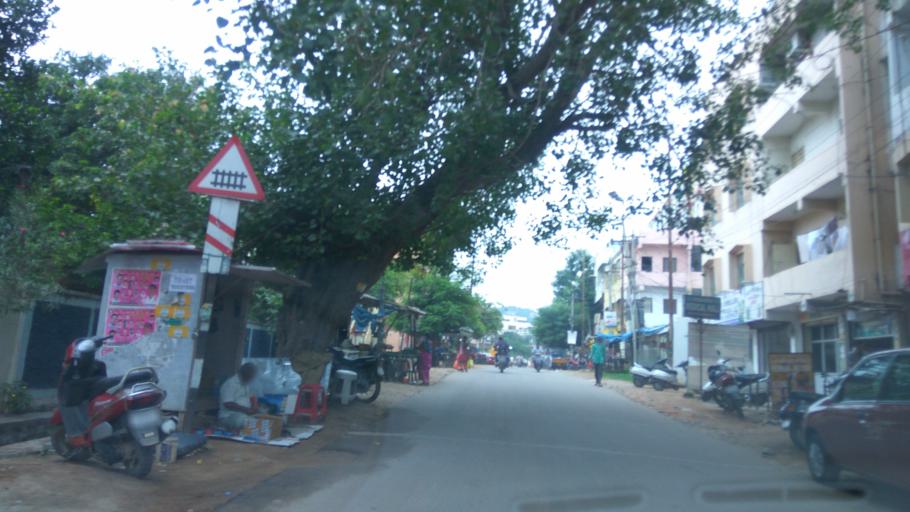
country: IN
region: Telangana
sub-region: Hyderabad
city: Malkajgiri
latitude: 17.4507
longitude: 78.5320
